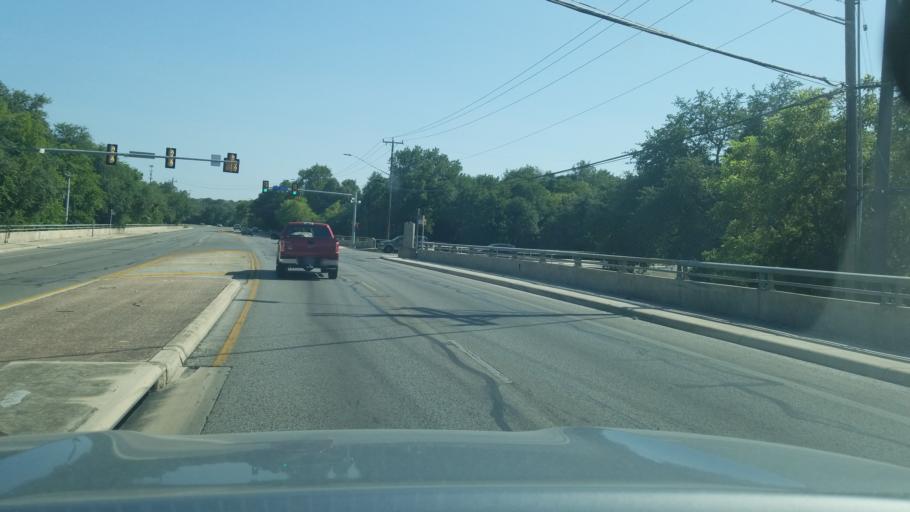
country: US
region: Texas
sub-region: Bexar County
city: Hollywood Park
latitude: 29.5866
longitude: -98.5155
